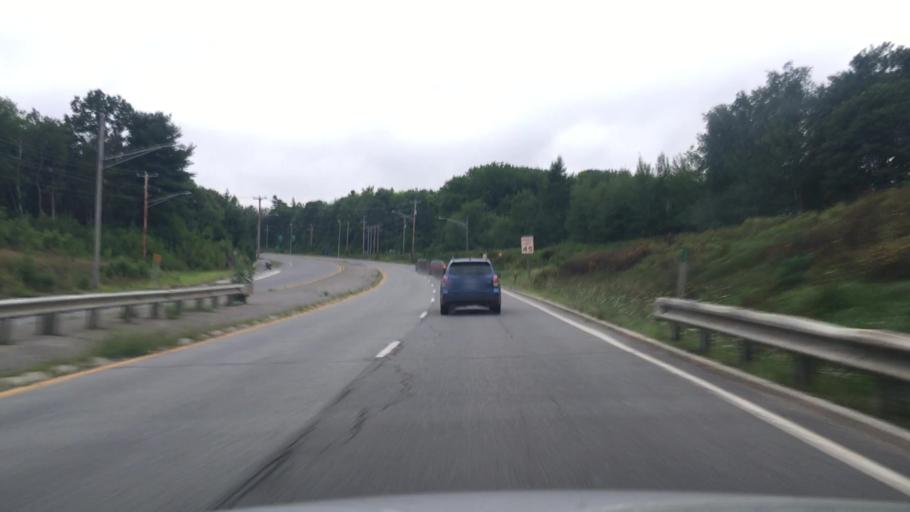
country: US
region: Maine
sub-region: Waldo County
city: Belfast
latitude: 44.4312
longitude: -69.0180
